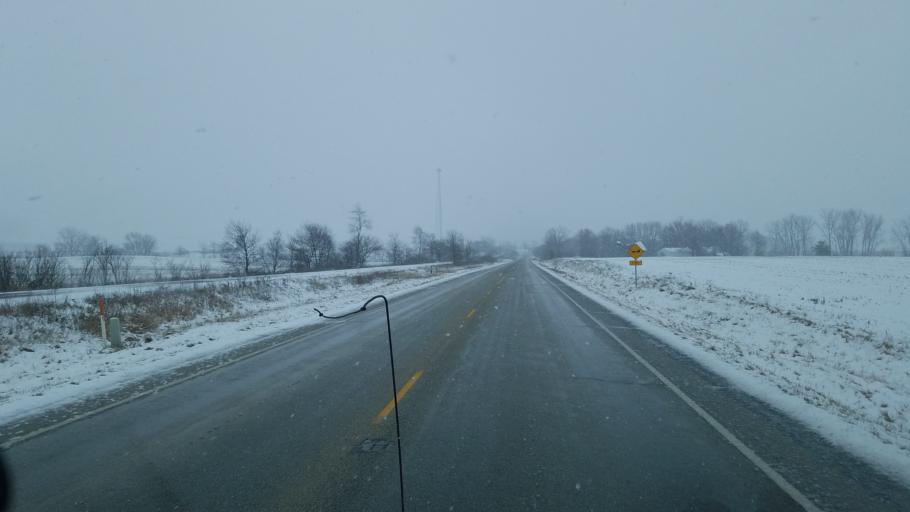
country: US
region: Indiana
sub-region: Randolph County
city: Lynn
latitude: 39.9708
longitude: -85.0394
